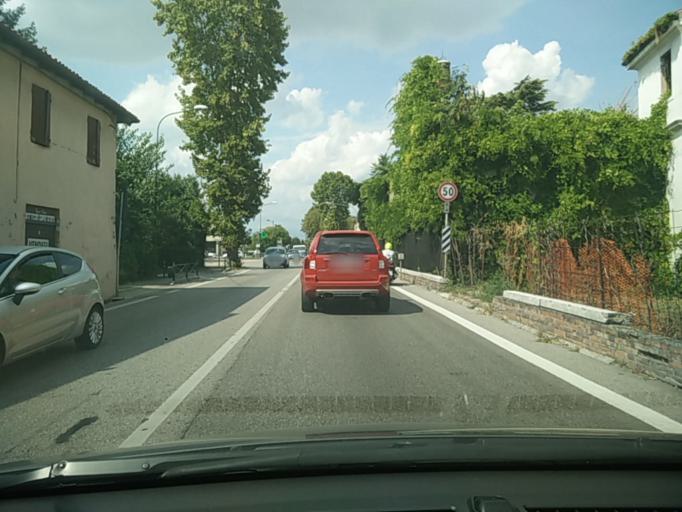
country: IT
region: Veneto
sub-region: Provincia di Treviso
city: Lancenigo-Villorba
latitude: 45.7128
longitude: 12.2593
